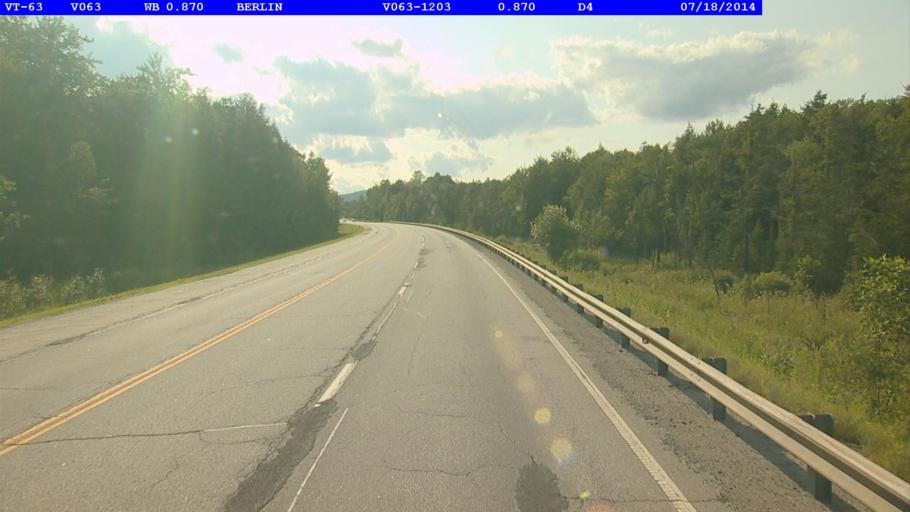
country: US
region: Vermont
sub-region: Orange County
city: Williamstown
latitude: 44.1668
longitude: -72.5602
